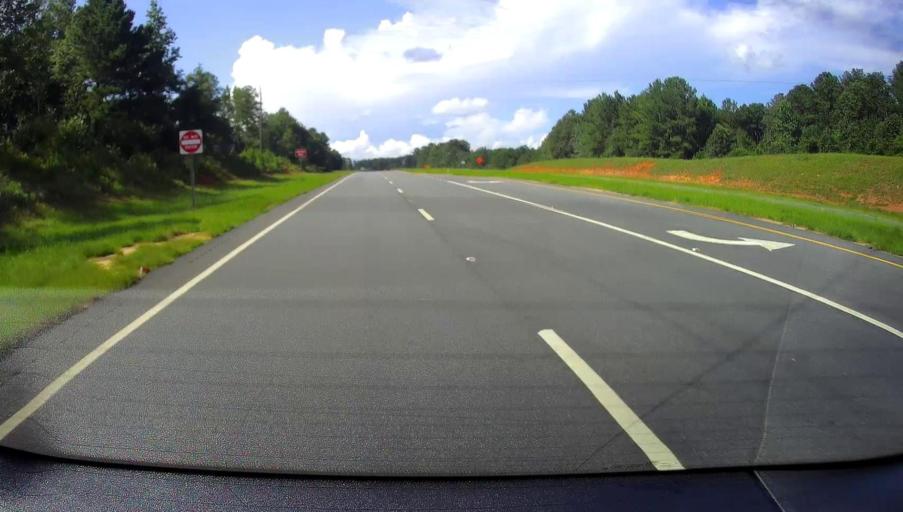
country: US
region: Georgia
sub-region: Upson County
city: Thomaston
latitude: 32.8549
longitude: -84.3171
